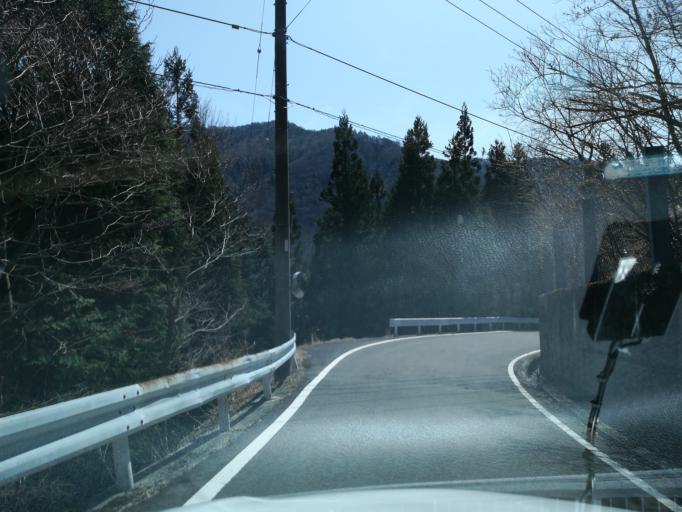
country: JP
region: Tokushima
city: Wakimachi
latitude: 33.8650
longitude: 134.0691
